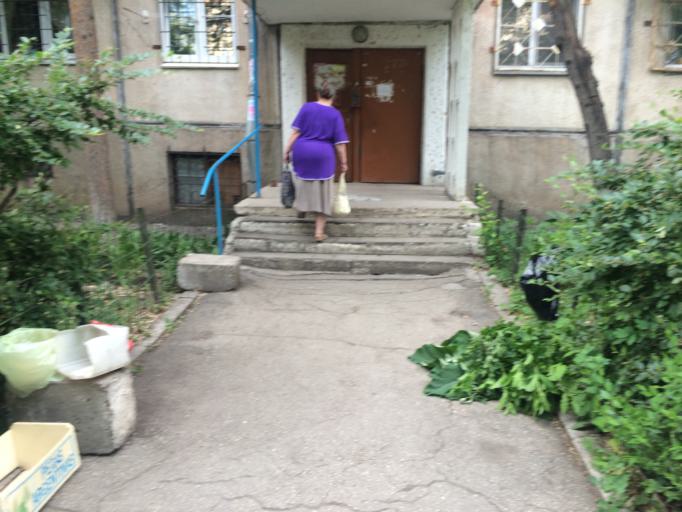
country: RU
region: Chelyabinsk
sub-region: Gorod Magnitogorsk
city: Magnitogorsk
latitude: 53.4042
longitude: 58.9835
